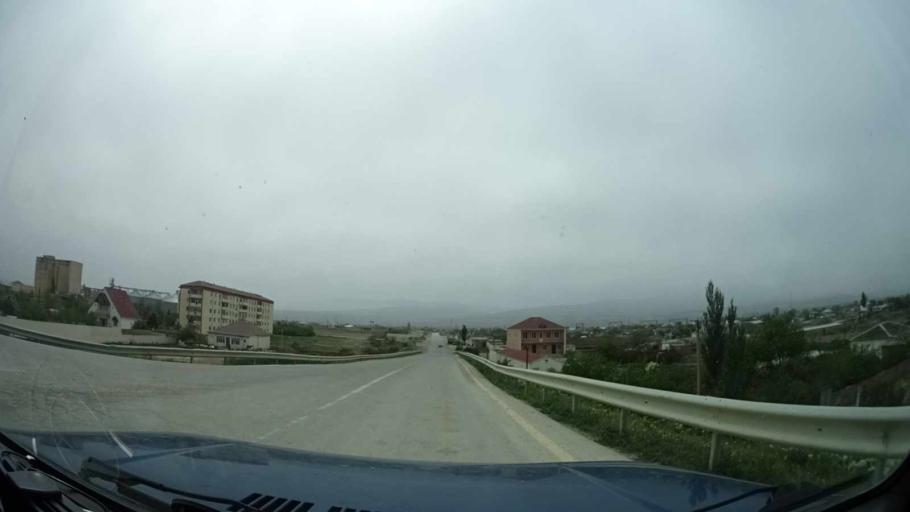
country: AZ
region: Xizi
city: Kilyazi
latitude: 40.8691
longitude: 49.3535
